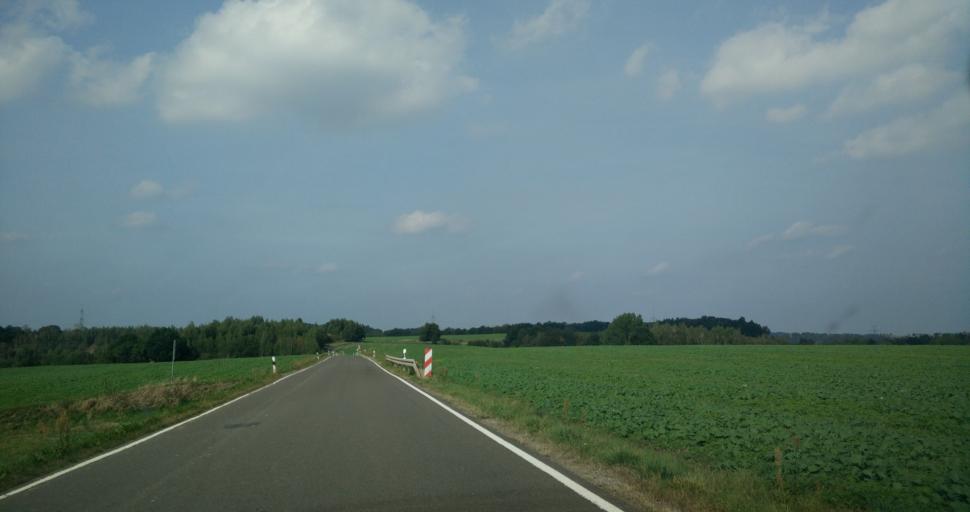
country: DE
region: Saxony
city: Colditz
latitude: 51.0963
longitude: 12.7973
